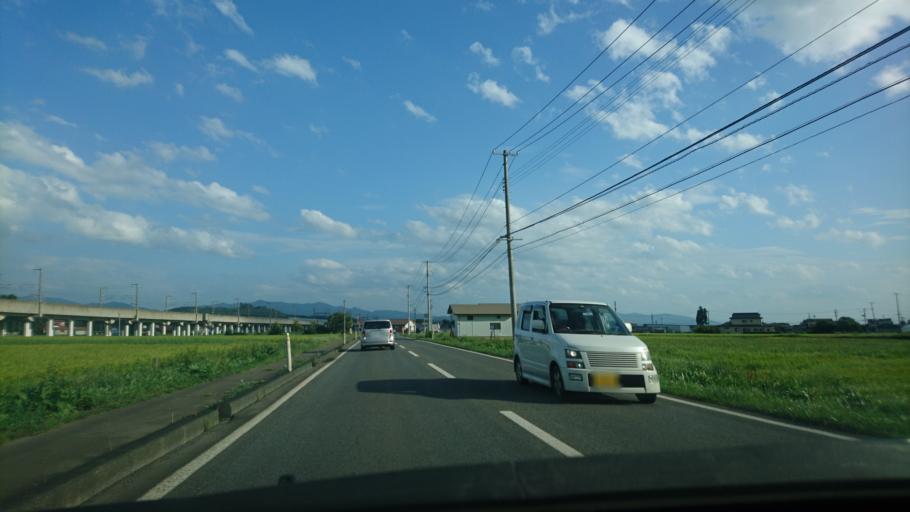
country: JP
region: Iwate
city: Mizusawa
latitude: 39.1672
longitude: 141.1795
